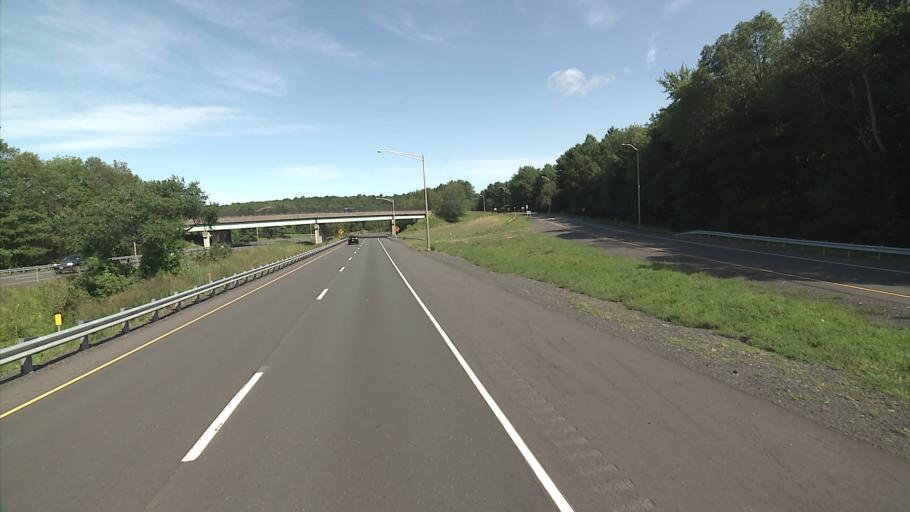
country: US
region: Connecticut
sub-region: Hartford County
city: Glastonbury Center
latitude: 41.6762
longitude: -72.5396
